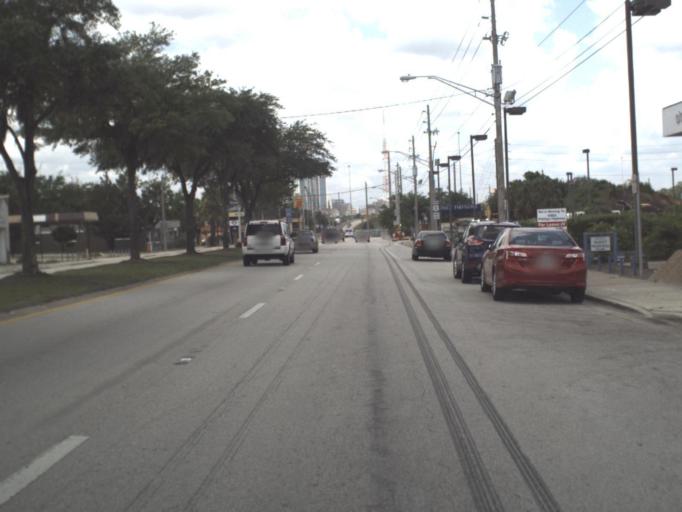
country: US
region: Florida
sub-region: Duval County
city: Jacksonville
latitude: 30.3030
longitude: -81.6437
